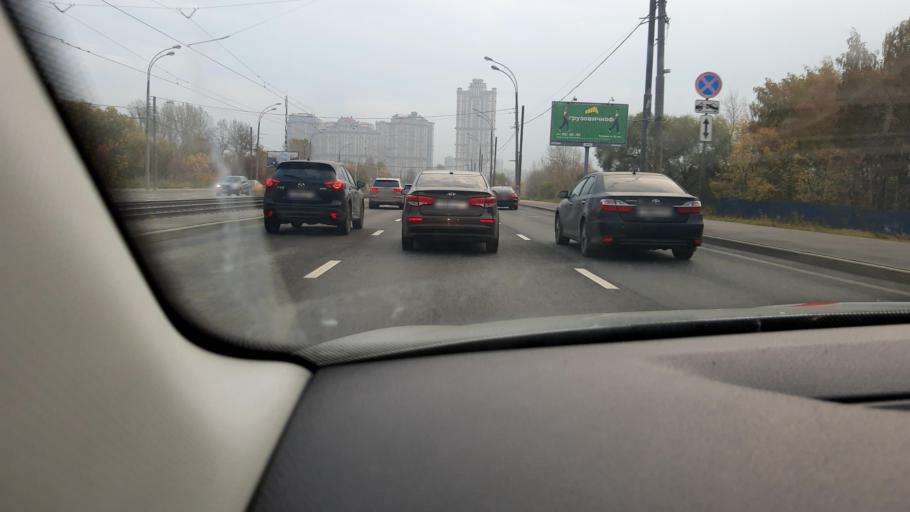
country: RU
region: Moscow
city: Shchukino
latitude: 55.8037
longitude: 37.4309
